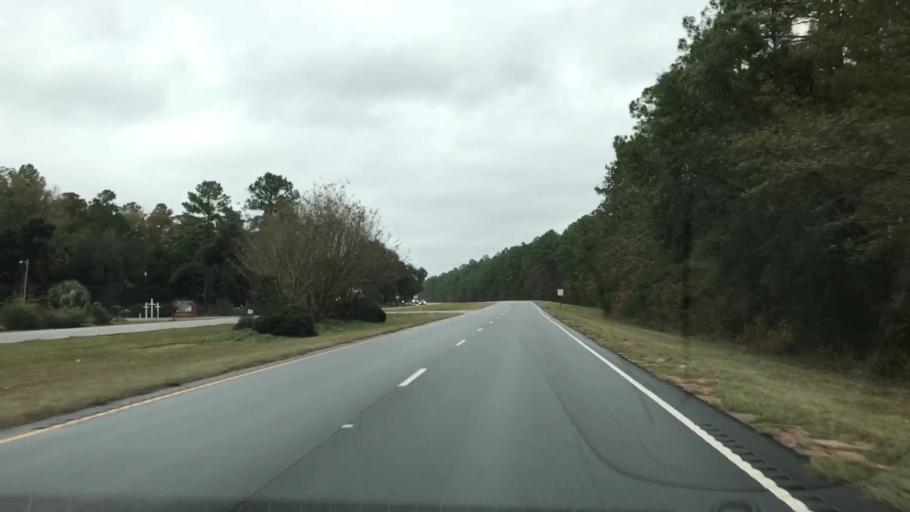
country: US
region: South Carolina
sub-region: Georgetown County
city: Georgetown
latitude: 33.2295
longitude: -79.3766
